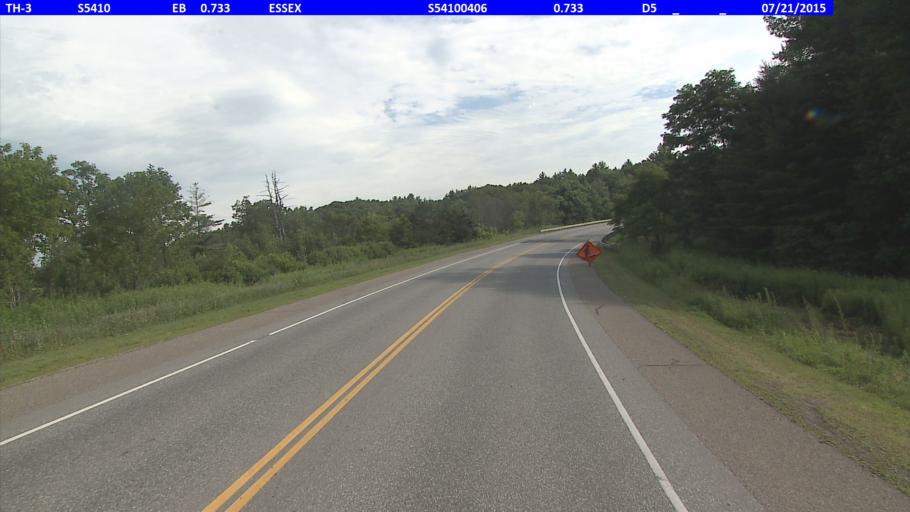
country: US
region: Vermont
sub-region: Chittenden County
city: Essex Junction
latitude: 44.5133
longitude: -73.1315
